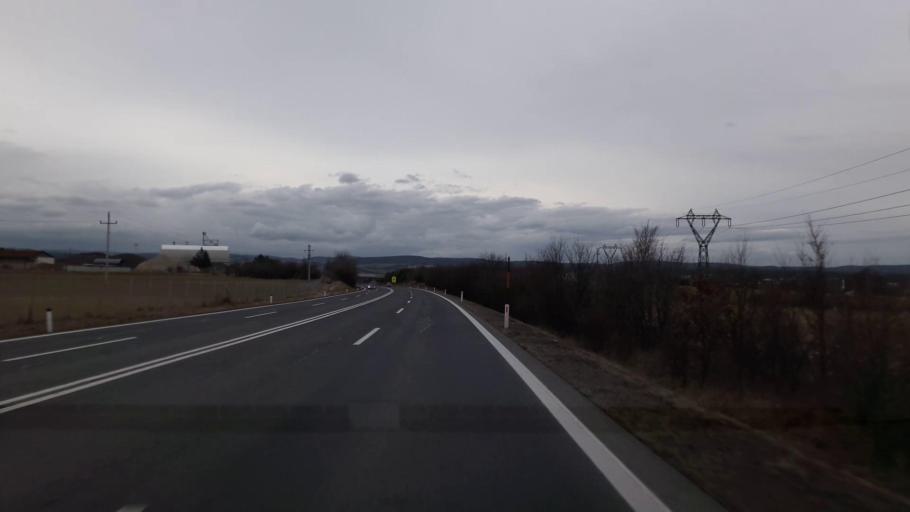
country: AT
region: Burgenland
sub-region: Politischer Bezirk Oberpullendorf
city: Markt Sankt Martin
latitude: 47.5515
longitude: 16.4188
